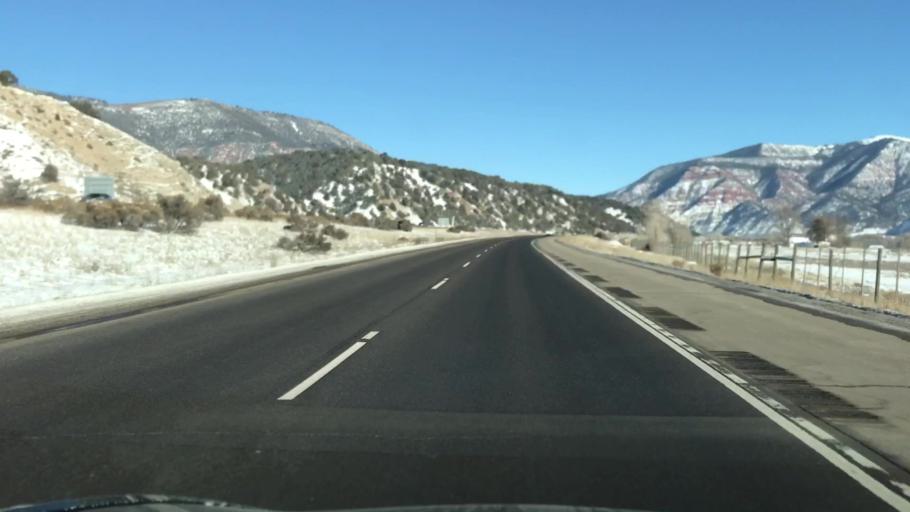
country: US
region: Colorado
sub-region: Eagle County
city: Eagle
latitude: 39.6714
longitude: -106.8029
